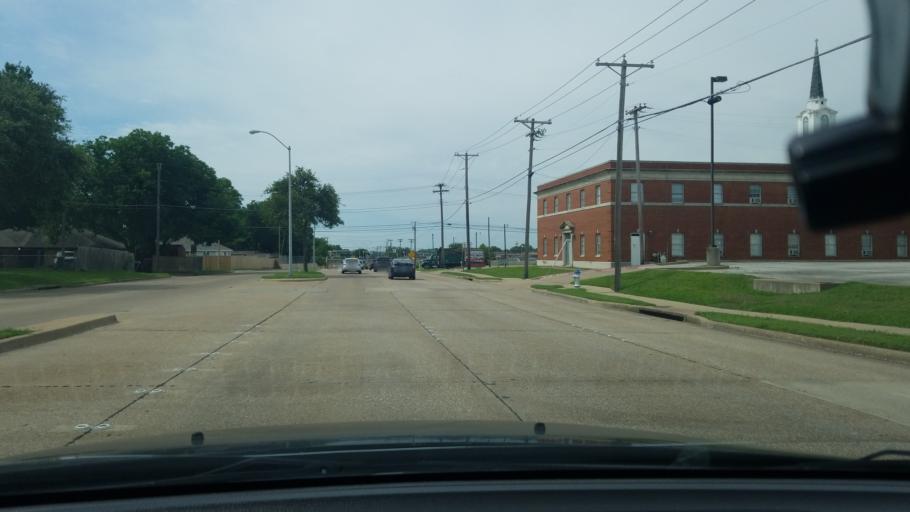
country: US
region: Texas
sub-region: Dallas County
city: Mesquite
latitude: 32.7696
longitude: -96.5971
